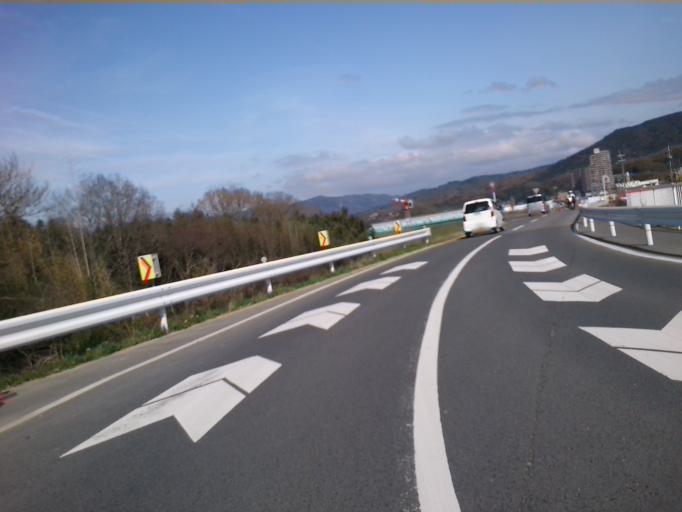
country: JP
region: Nara
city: Nara-shi
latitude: 34.7527
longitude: 135.8597
